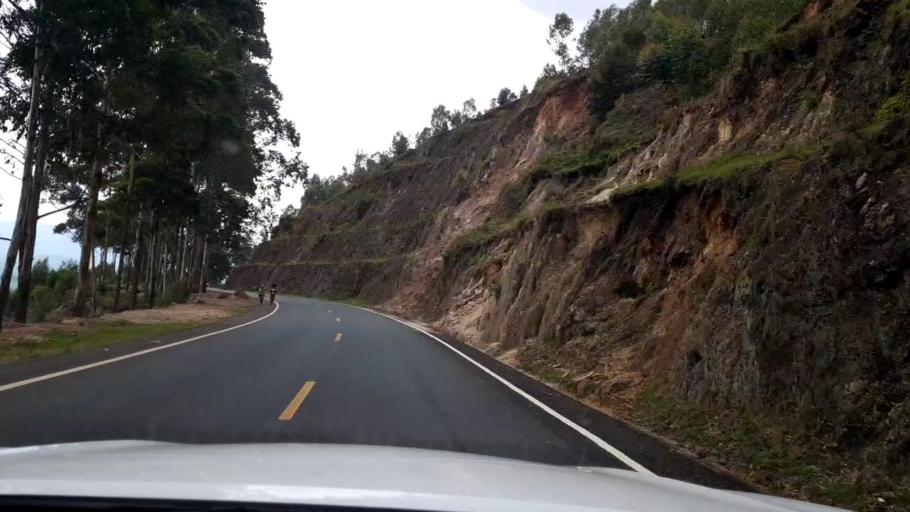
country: RW
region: Southern Province
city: Gitarama
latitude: -2.0248
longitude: 29.7167
